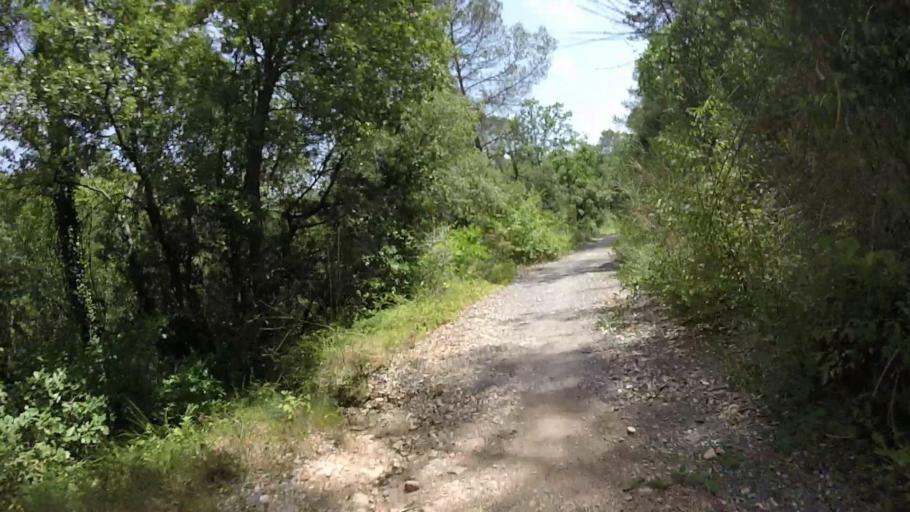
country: FR
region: Provence-Alpes-Cote d'Azur
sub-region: Departement des Alpes-Maritimes
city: Mougins
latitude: 43.6196
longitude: 7.0287
